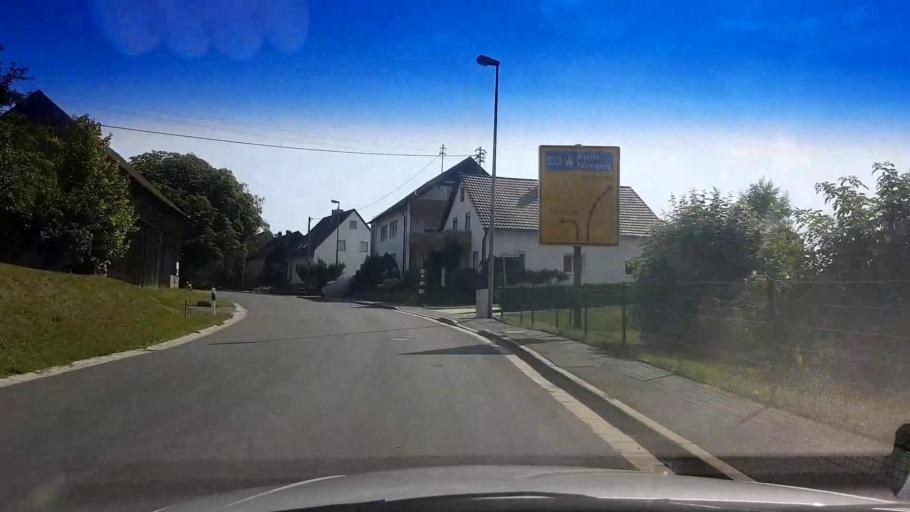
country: DE
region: Bavaria
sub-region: Upper Franconia
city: Mistelgau
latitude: 49.9439
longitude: 11.4430
